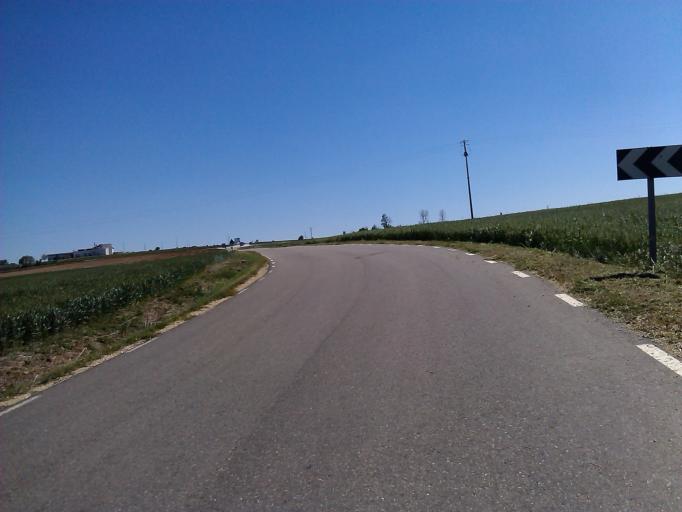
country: ES
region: Castille and Leon
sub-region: Provincia de Burgos
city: Arlanzon
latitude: 42.3551
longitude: -3.4629
